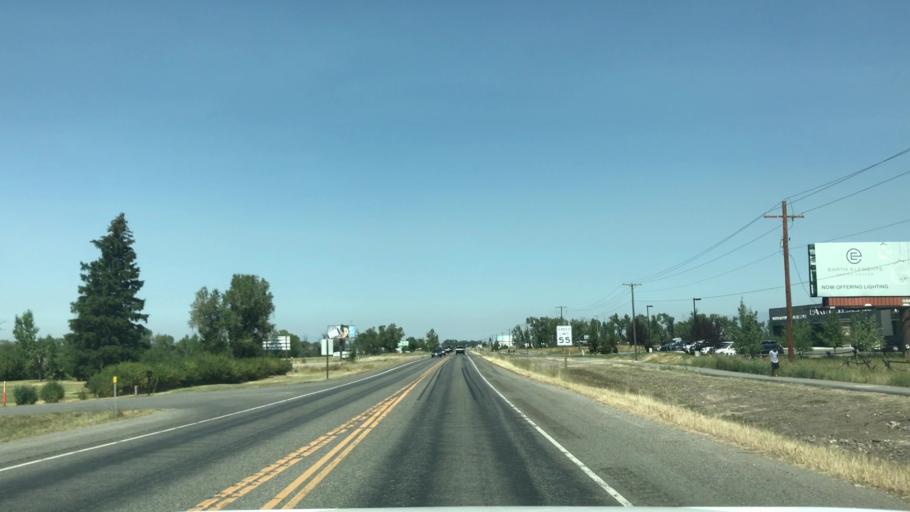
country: US
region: Montana
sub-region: Gallatin County
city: Four Corners
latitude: 45.5933
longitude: -111.1969
